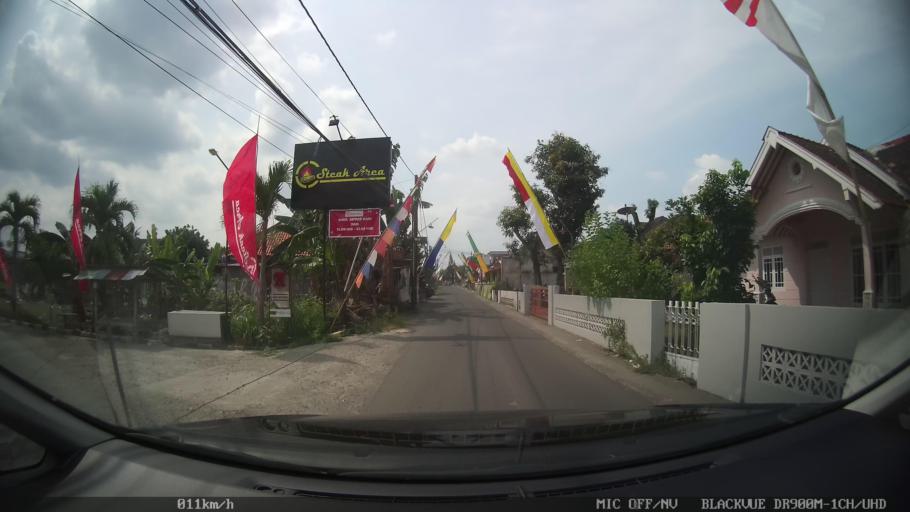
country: ID
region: Daerah Istimewa Yogyakarta
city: Depok
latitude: -7.7873
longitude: 110.4055
